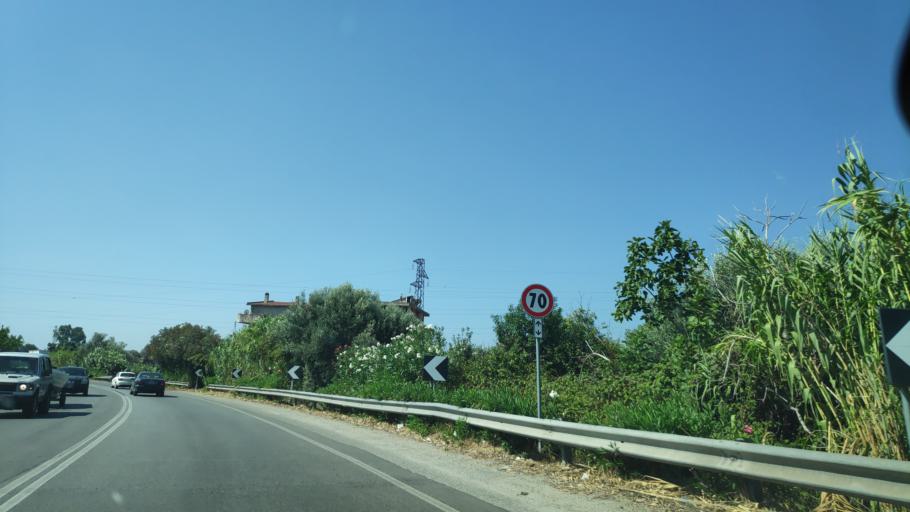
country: IT
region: Calabria
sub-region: Provincia di Reggio Calabria
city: Bovalino
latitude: 38.1501
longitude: 16.1685
